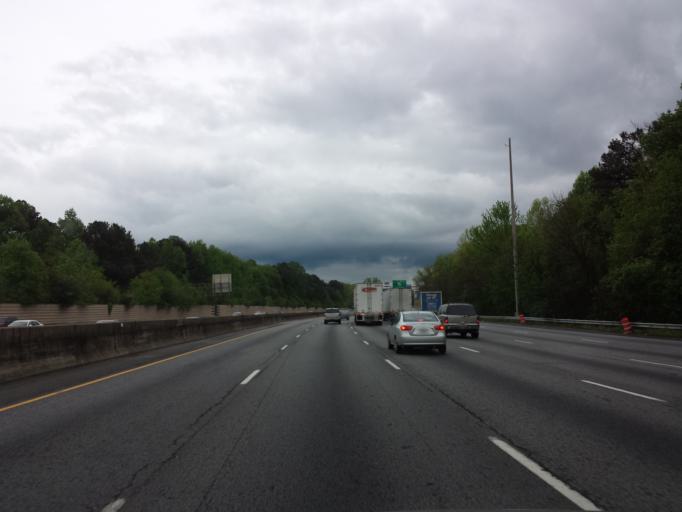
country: US
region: Georgia
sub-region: Cobb County
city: Smyrna
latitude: 33.9328
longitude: -84.4920
